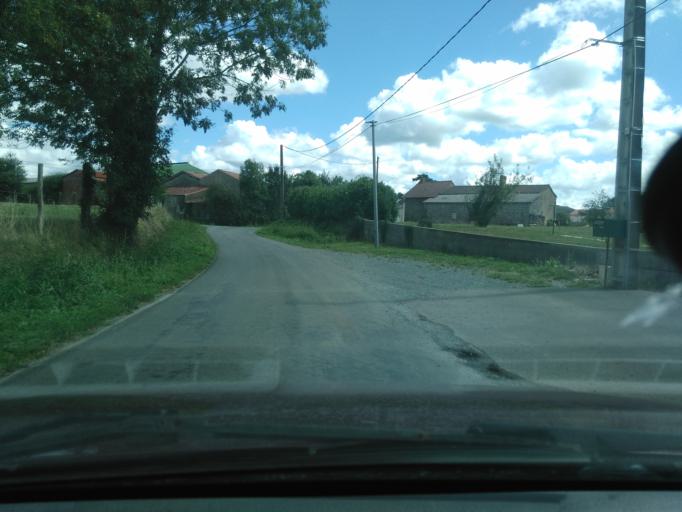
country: FR
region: Pays de la Loire
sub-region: Departement de la Vendee
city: La Ferriere
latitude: 46.7426
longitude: -1.3118
